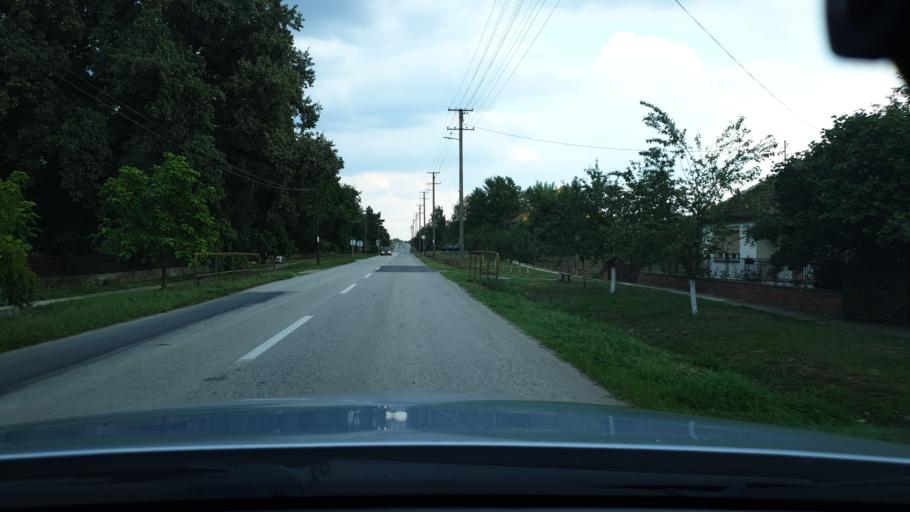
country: RS
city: Konak
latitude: 45.3107
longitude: 20.9112
